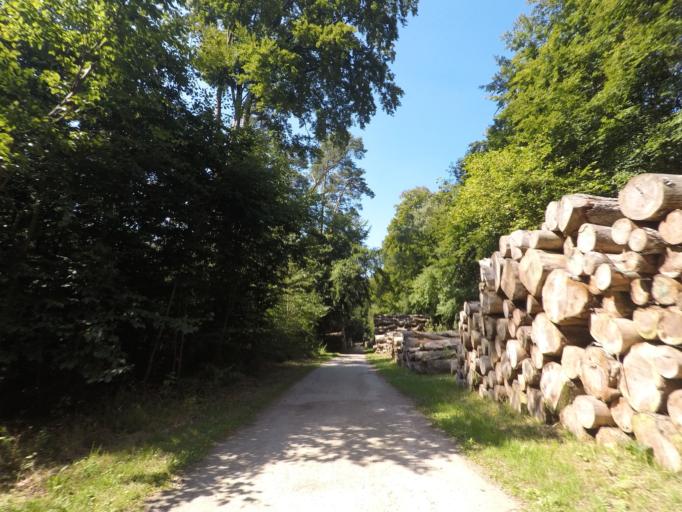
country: LU
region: Luxembourg
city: Bridel
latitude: 49.6460
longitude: 6.0923
